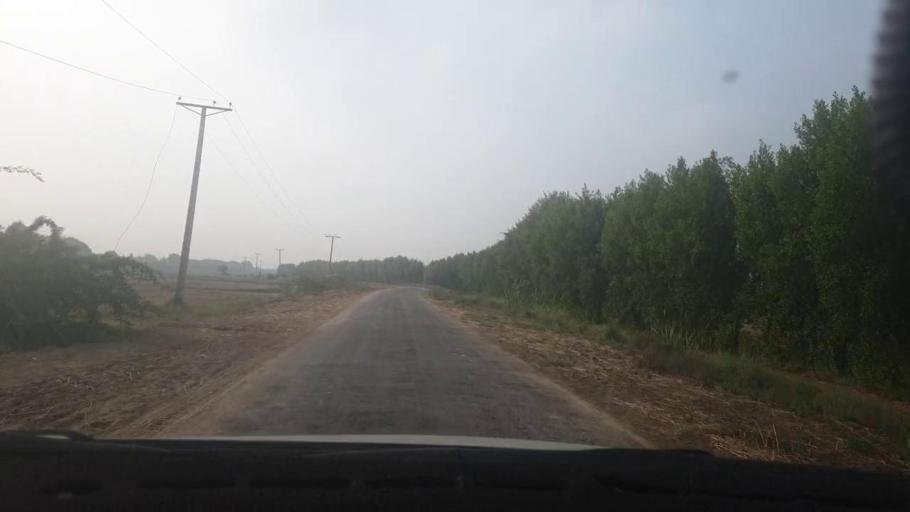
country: PK
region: Sindh
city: Tando Muhammad Khan
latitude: 25.1000
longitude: 68.5162
